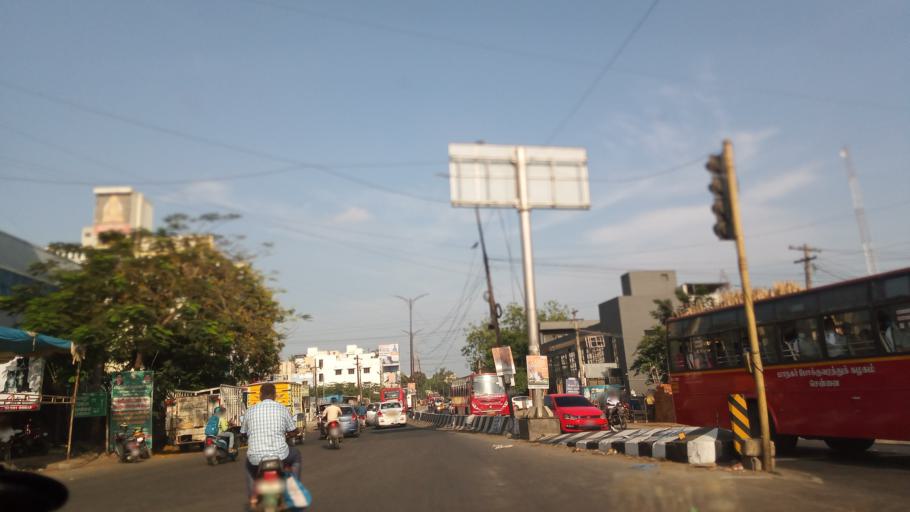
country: IN
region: Tamil Nadu
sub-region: Kancheepuram
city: Poonamalle
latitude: 13.0452
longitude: 80.1172
